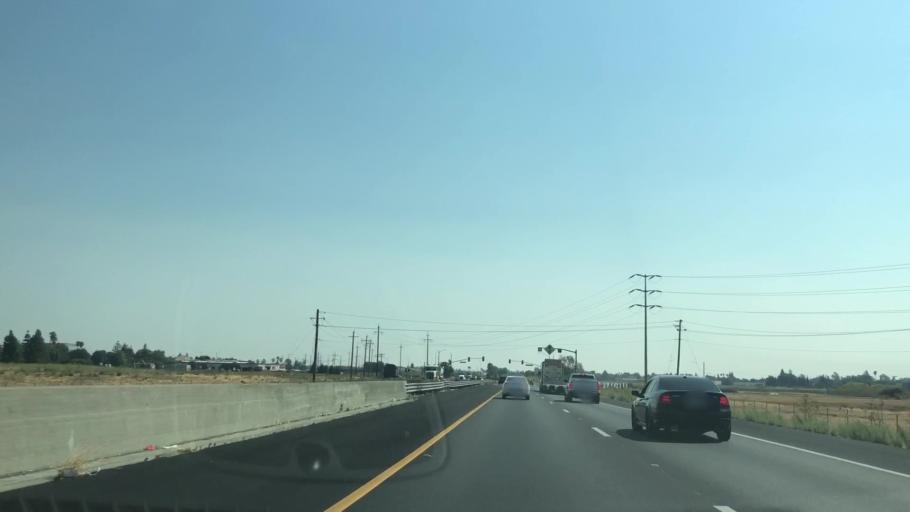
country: US
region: California
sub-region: Solano County
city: Suisun
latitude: 38.2408
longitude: -122.0536
